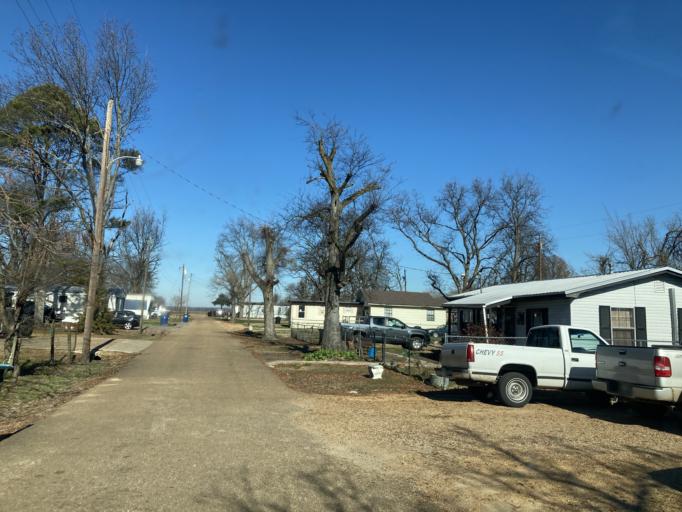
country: US
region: Mississippi
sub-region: Yazoo County
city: Yazoo City
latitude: 32.9782
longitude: -90.5942
